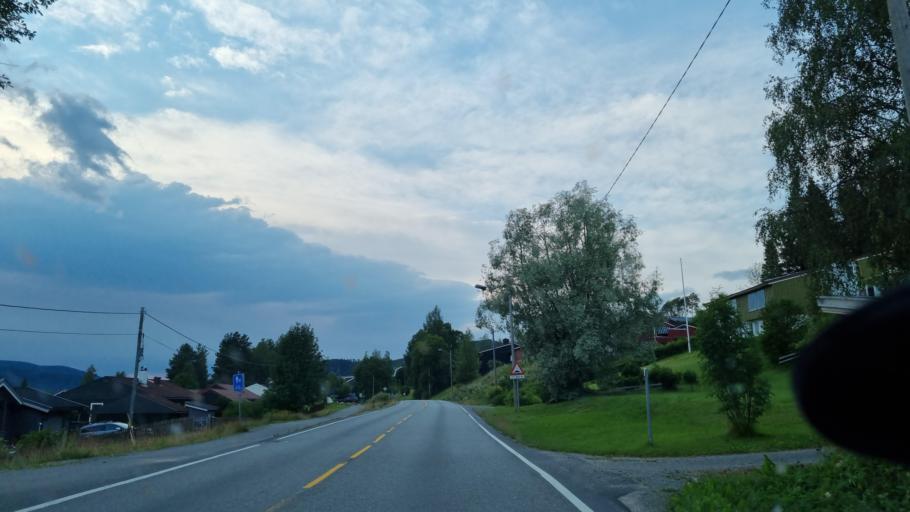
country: NO
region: Hedmark
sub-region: Trysil
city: Innbygda
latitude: 61.3092
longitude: 12.2723
